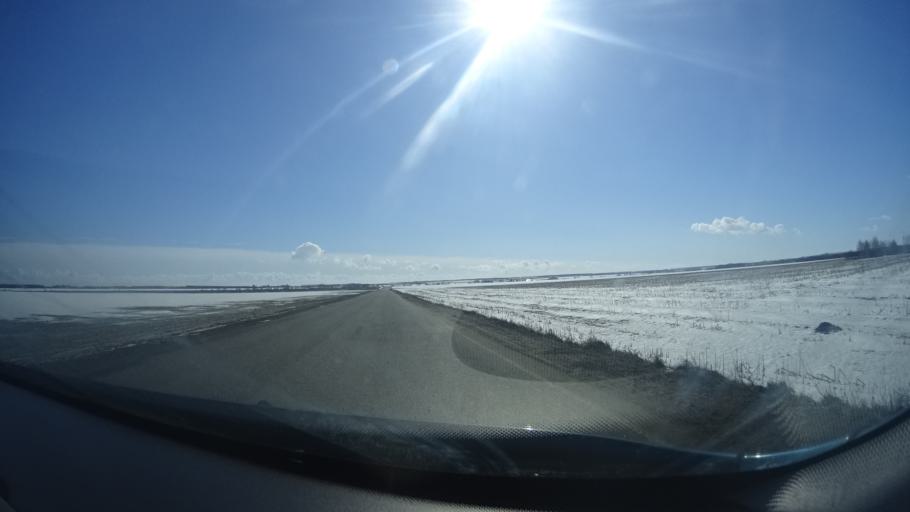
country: RU
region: Bashkortostan
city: Avdon
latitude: 54.6002
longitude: 55.8505
